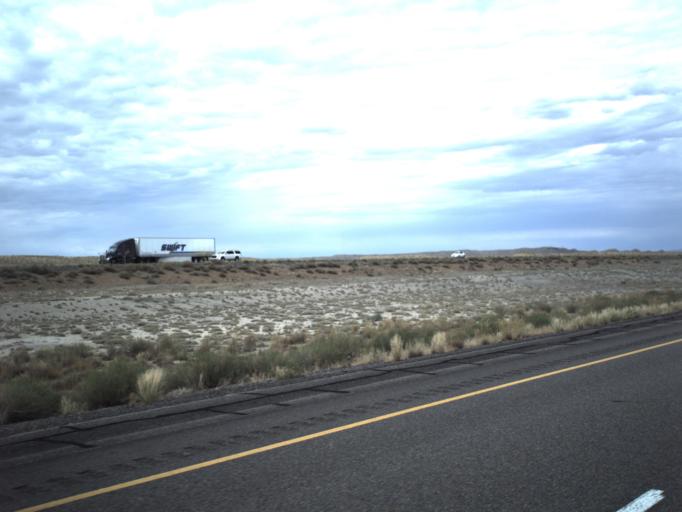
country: US
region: Utah
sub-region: Grand County
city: Moab
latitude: 38.9418
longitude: -109.5481
